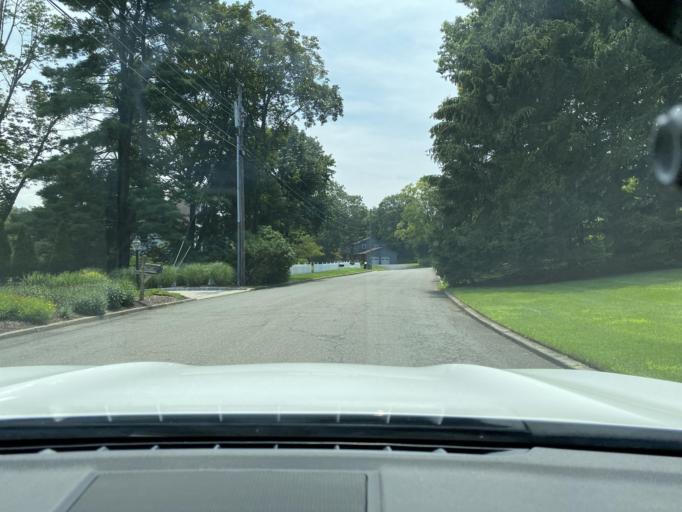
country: US
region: New Jersey
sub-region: Bergen County
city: Upper Saddle River
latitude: 41.0789
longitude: -74.1046
